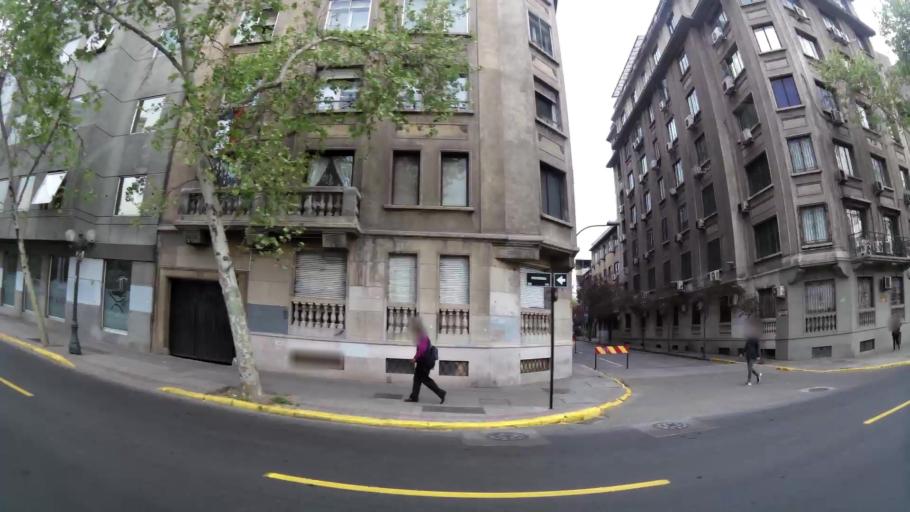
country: CL
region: Santiago Metropolitan
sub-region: Provincia de Santiago
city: Santiago
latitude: -33.4313
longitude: -70.6237
